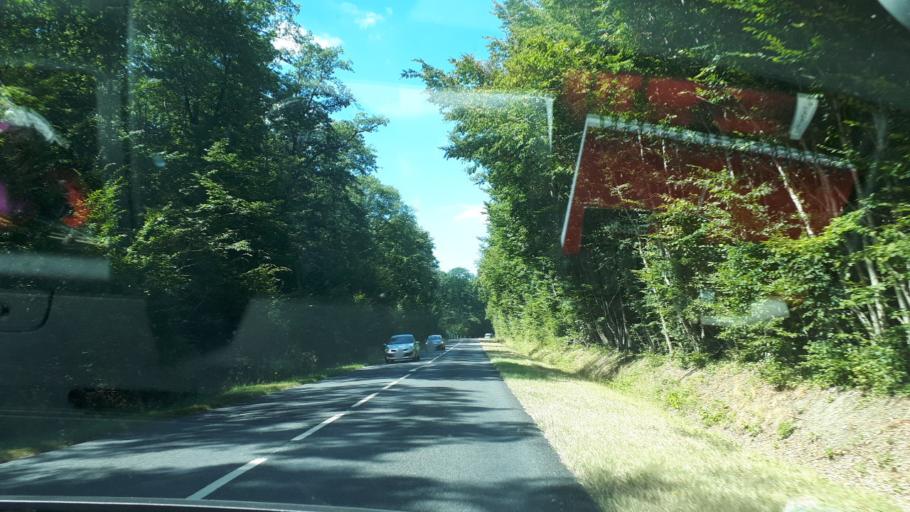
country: FR
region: Centre
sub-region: Departement du Loir-et-Cher
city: Mont-pres-Chambord
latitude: 47.5618
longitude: 1.4905
